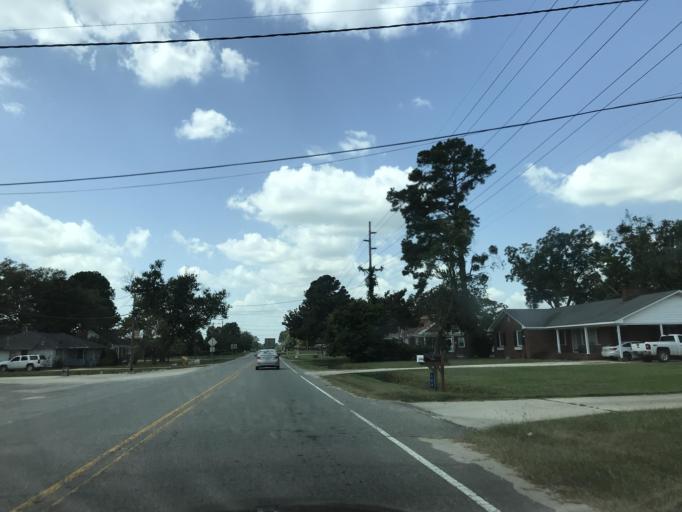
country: US
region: North Carolina
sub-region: Sampson County
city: Plain View
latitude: 35.2459
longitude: -78.3561
